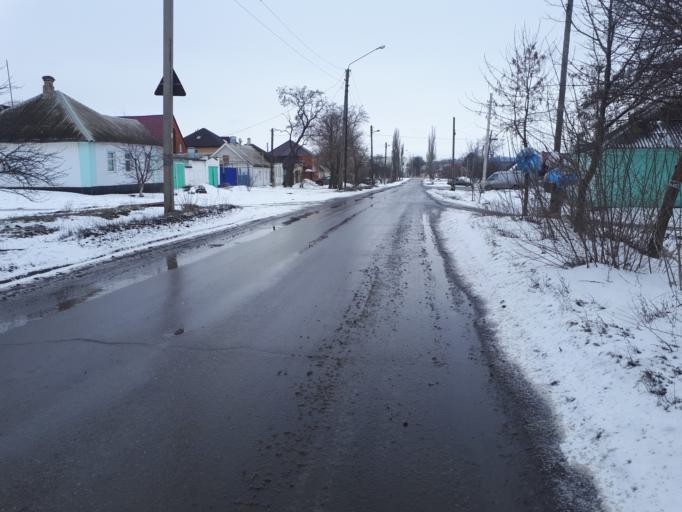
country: RU
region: Rostov
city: Krasnyy Sulin
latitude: 47.8995
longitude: 40.0551
